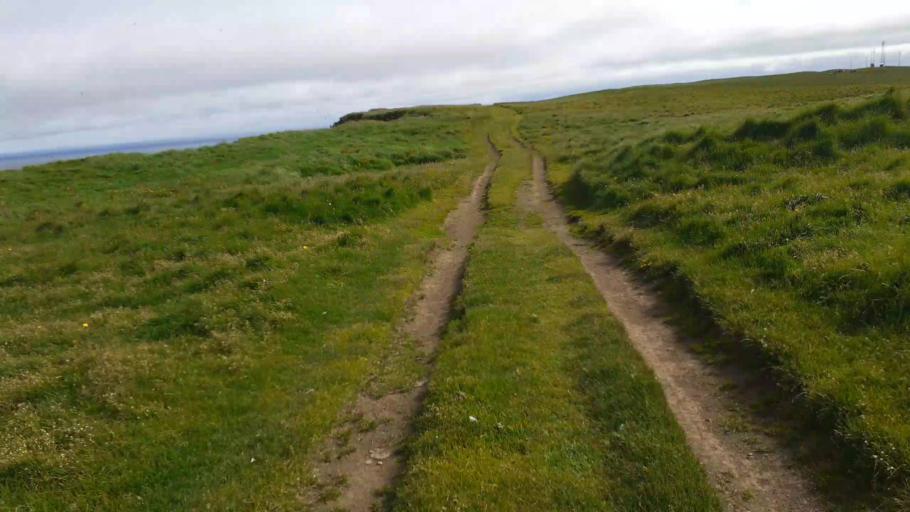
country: IS
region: Northeast
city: Dalvik
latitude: 66.5526
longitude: -17.9971
